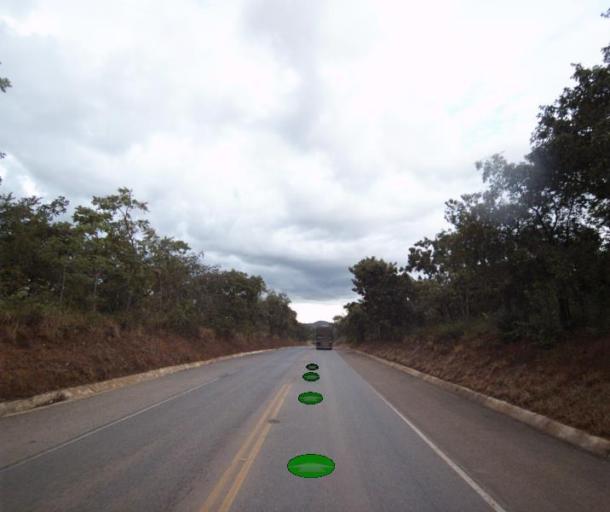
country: BR
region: Goias
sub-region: Uruacu
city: Uruacu
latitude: -14.7446
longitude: -49.2493
